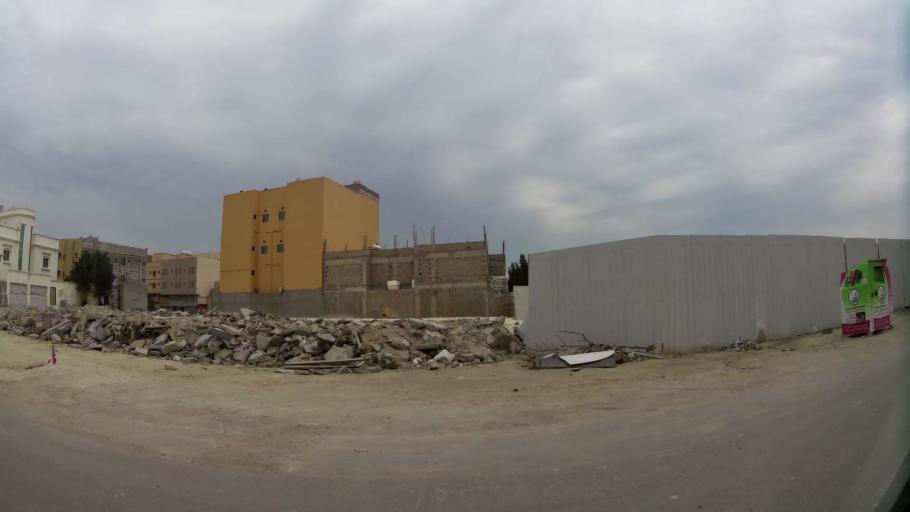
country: BH
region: Northern
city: Sitrah
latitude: 26.1689
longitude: 50.6115
